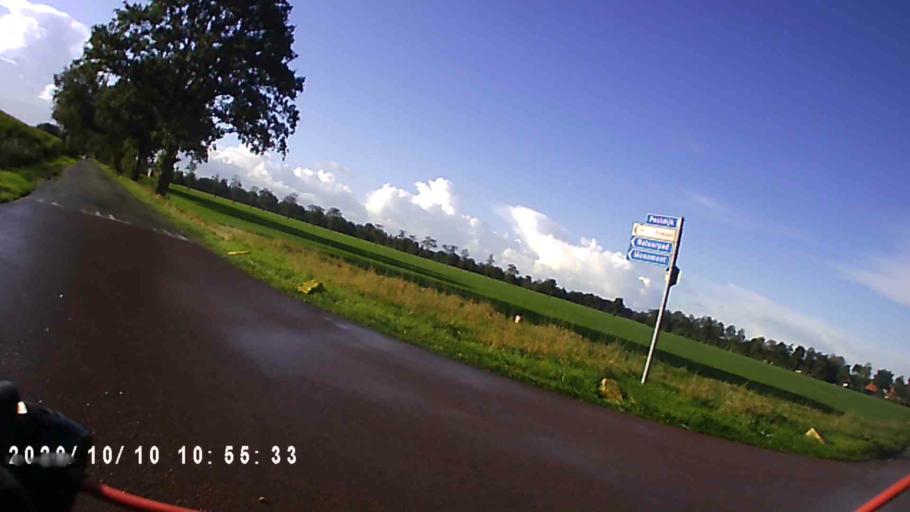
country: NL
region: Friesland
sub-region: Gemeente Achtkarspelen
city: Surhuisterveen
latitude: 53.1545
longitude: 6.2068
